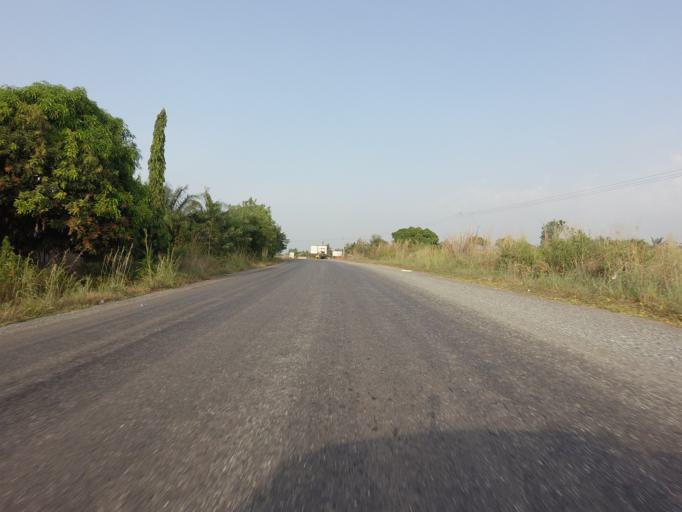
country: GH
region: Volta
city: Ho
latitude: 6.4416
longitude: 0.2062
